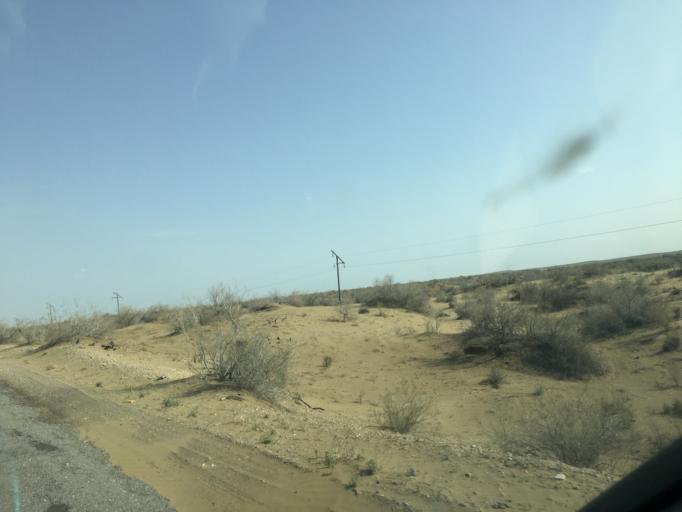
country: TM
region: Lebap
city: Farap
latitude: 39.3279
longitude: 63.3366
